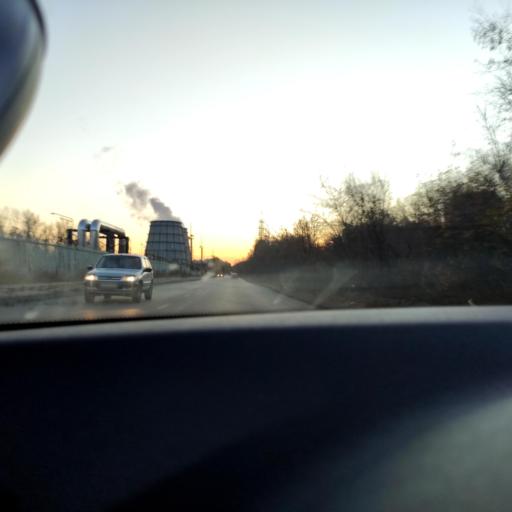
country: RU
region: Samara
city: Petra-Dubrava
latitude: 53.2548
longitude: 50.2780
